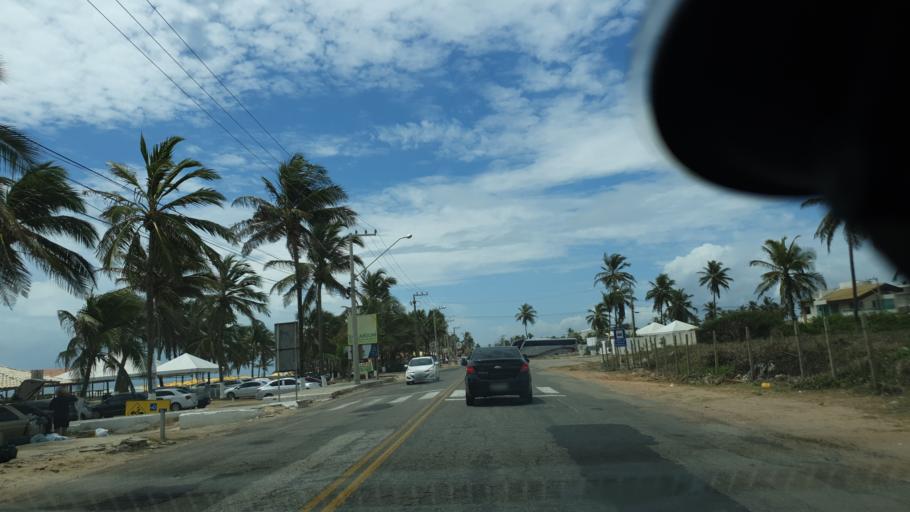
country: BR
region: Sergipe
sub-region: Aracaju
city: Aracaju
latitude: -11.0294
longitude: -37.0781
